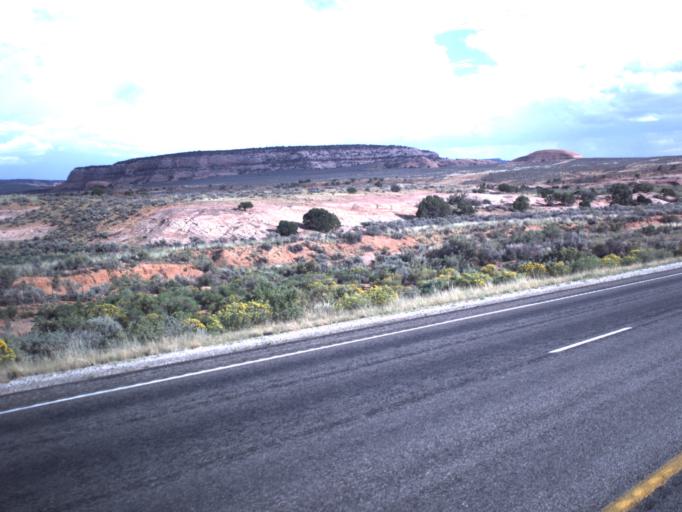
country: US
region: Utah
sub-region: San Juan County
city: Monticello
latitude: 38.2289
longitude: -109.3768
